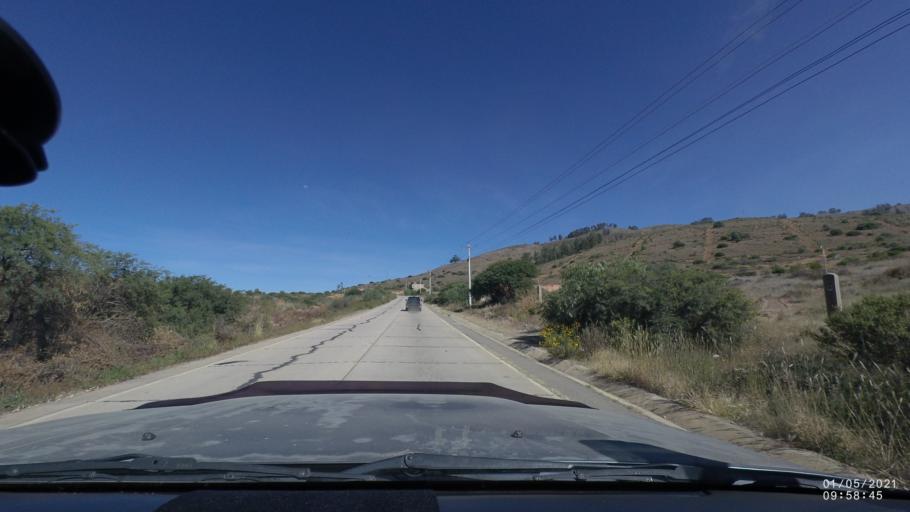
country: BO
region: Cochabamba
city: Cochabamba
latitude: -17.5239
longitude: -66.1829
